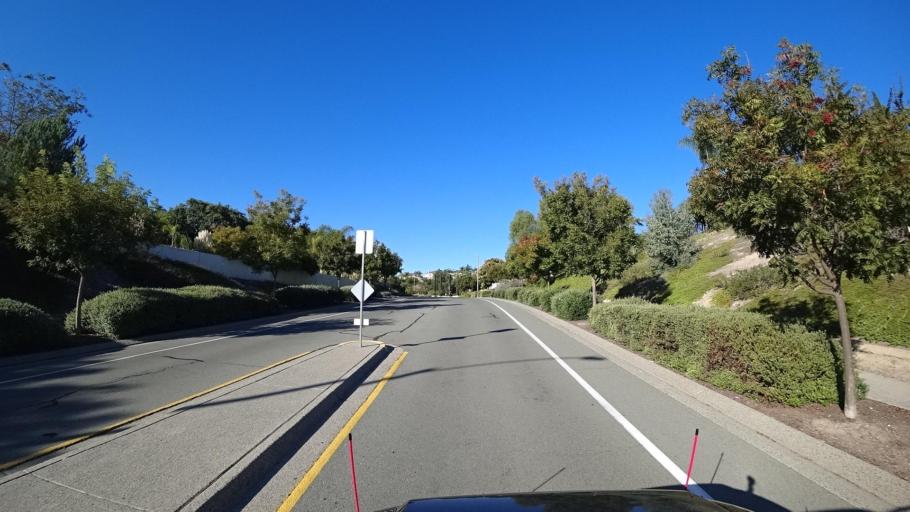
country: US
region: California
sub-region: San Diego County
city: La Presa
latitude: 32.6592
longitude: -116.9430
